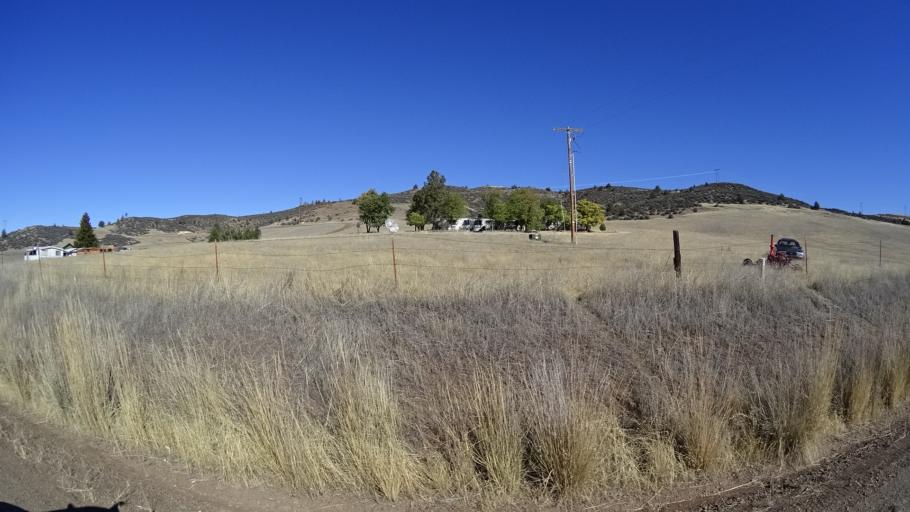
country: US
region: California
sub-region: Siskiyou County
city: Montague
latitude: 41.8663
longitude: -122.4524
